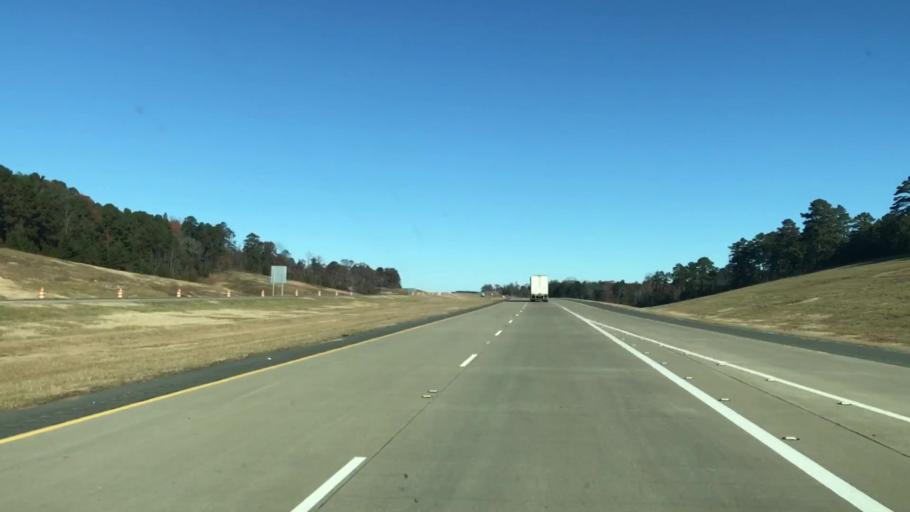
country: US
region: Louisiana
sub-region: Caddo Parish
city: Vivian
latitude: 32.9465
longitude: -93.8982
